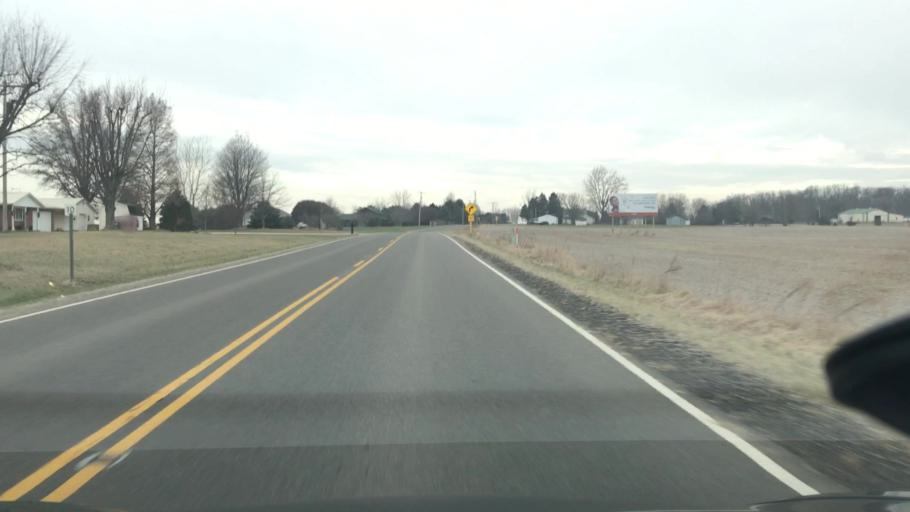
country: US
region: Ohio
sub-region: Madison County
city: London
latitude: 39.8657
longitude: -83.4162
